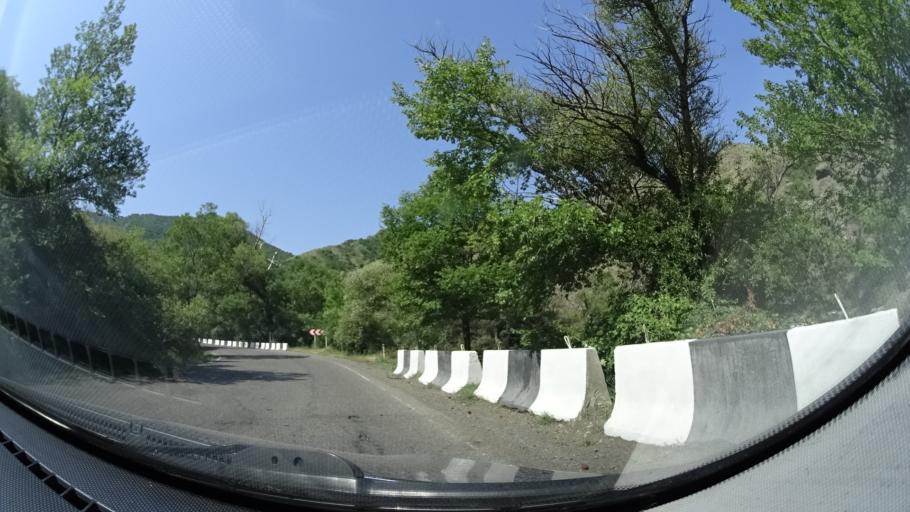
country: GE
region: Samtskhe-Javakheti
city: Akhaltsikhe
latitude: 41.6177
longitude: 43.0664
